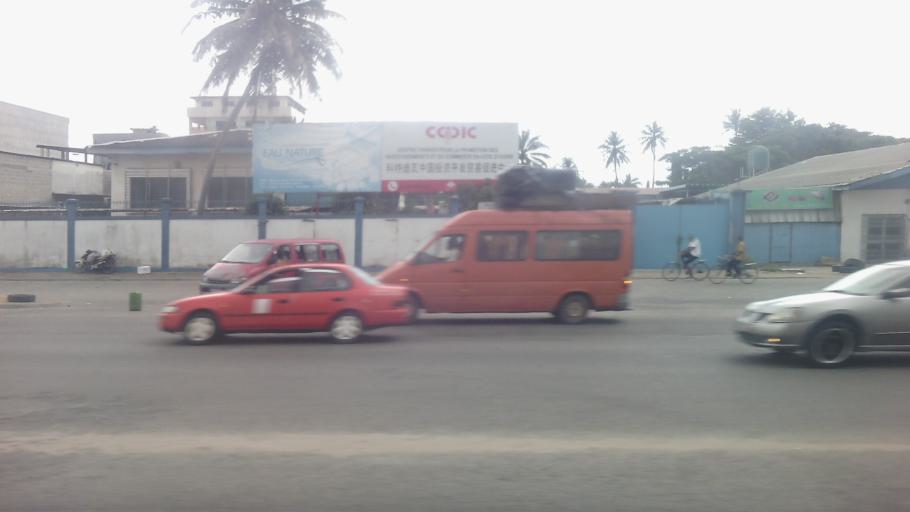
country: CI
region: Lagunes
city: Abidjan
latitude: 5.2920
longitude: -3.9738
